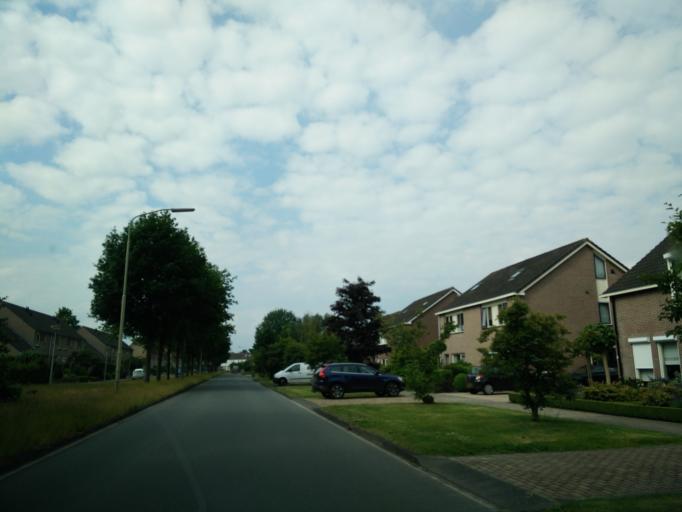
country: NL
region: Drenthe
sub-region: Gemeente Assen
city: Assen
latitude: 53.0226
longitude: 6.5850
